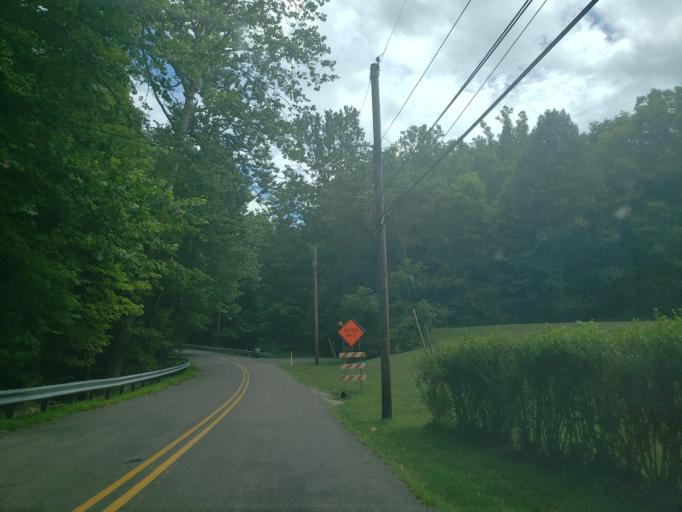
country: US
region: Pennsylvania
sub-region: Allegheny County
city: Coraopolis
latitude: 40.5359
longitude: -80.1313
